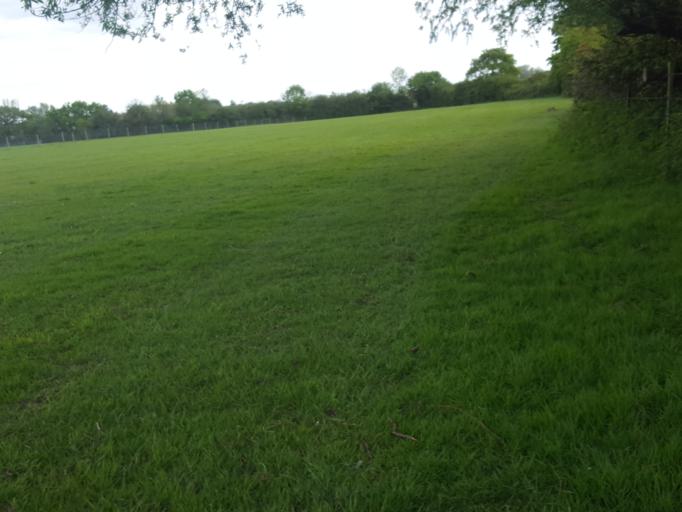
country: GB
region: England
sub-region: Essex
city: Frinton-on-Sea
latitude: 51.8404
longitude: 1.2078
